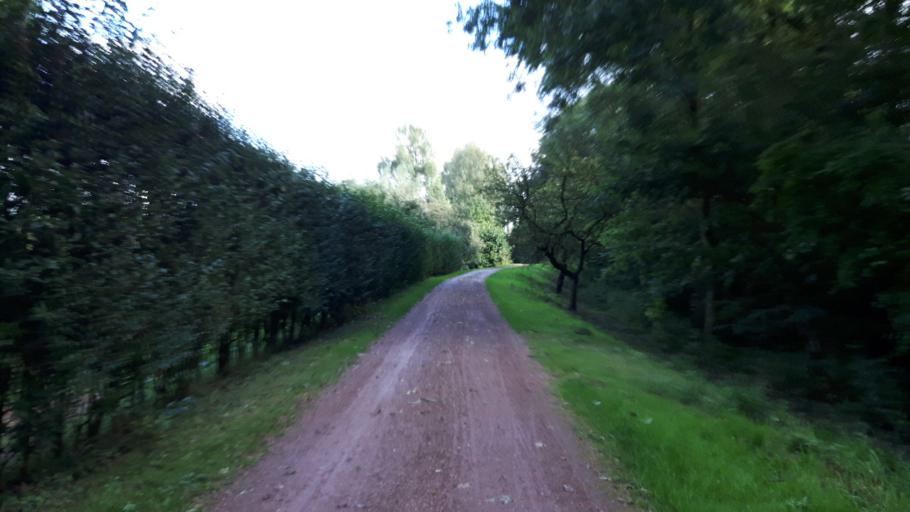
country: NL
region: South Holland
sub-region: Gemeente Leerdam
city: Leerdam
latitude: 51.8736
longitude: 5.0639
